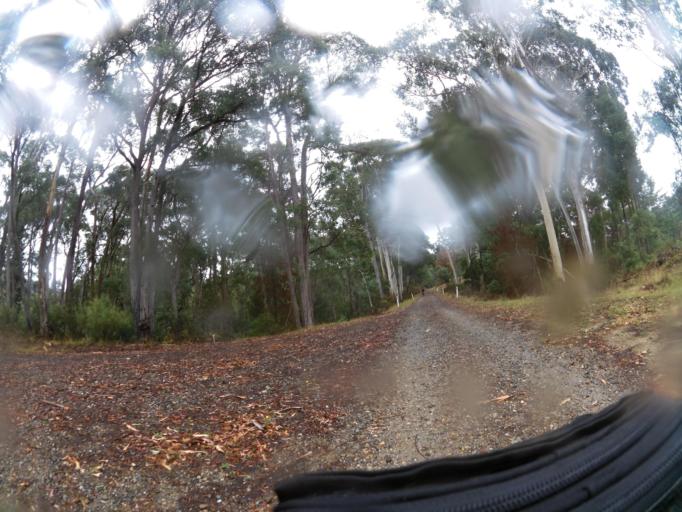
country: AU
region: New South Wales
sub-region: Greater Hume Shire
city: Holbrook
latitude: -36.2311
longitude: 147.5877
